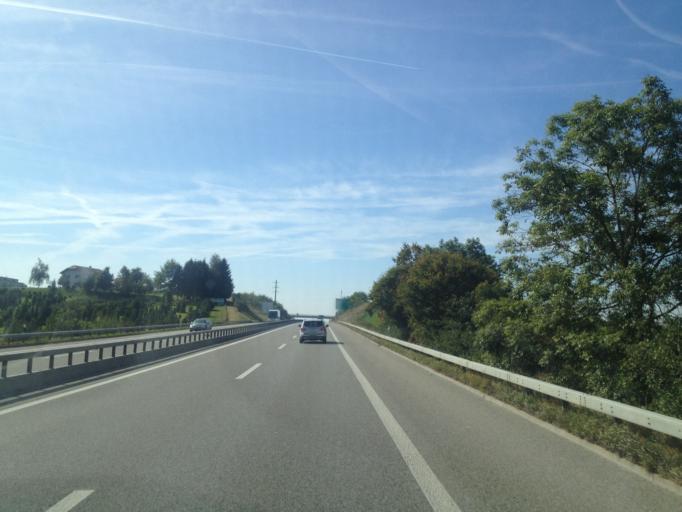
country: CH
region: Fribourg
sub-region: Sense District
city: Dudingen
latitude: 46.8518
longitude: 7.1826
